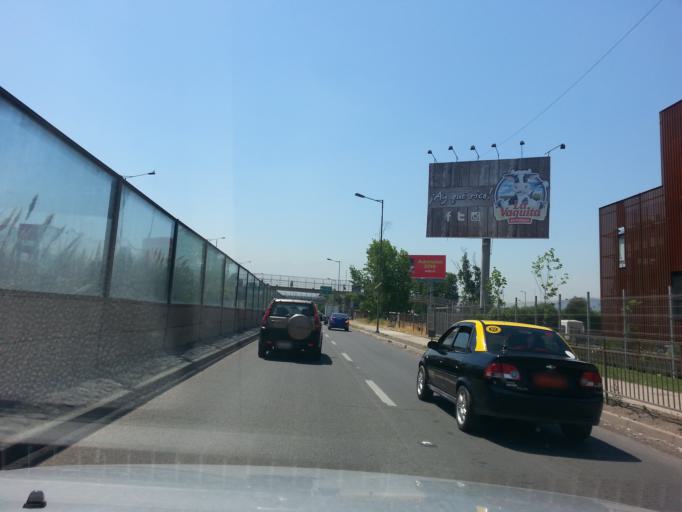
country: CL
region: Santiago Metropolitan
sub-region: Provincia de Chacabuco
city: Chicureo Abajo
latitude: -33.3676
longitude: -70.6807
